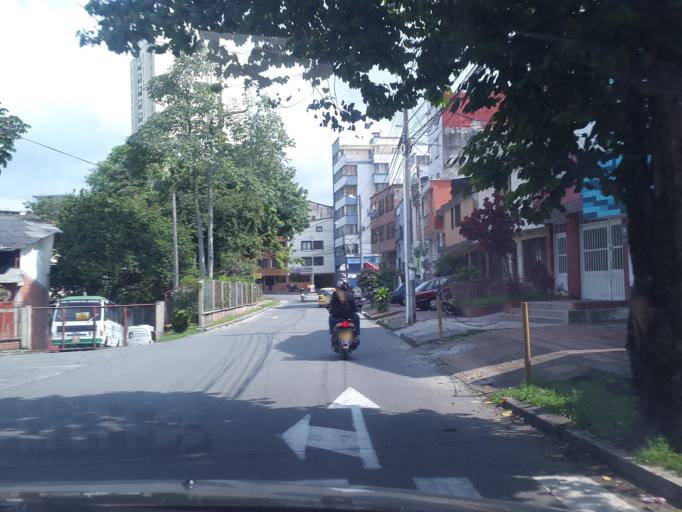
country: CO
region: Quindio
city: Armenia
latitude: 4.5528
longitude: -75.6588
